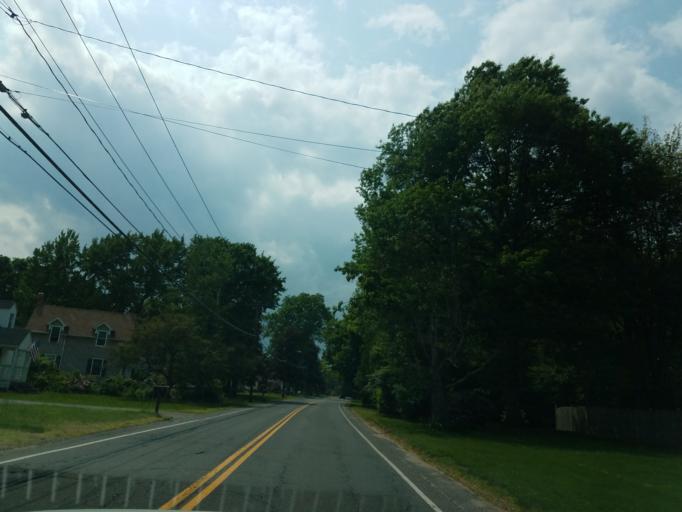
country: US
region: Massachusetts
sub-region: Hampden County
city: Agawam
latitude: 42.0427
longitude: -72.6237
